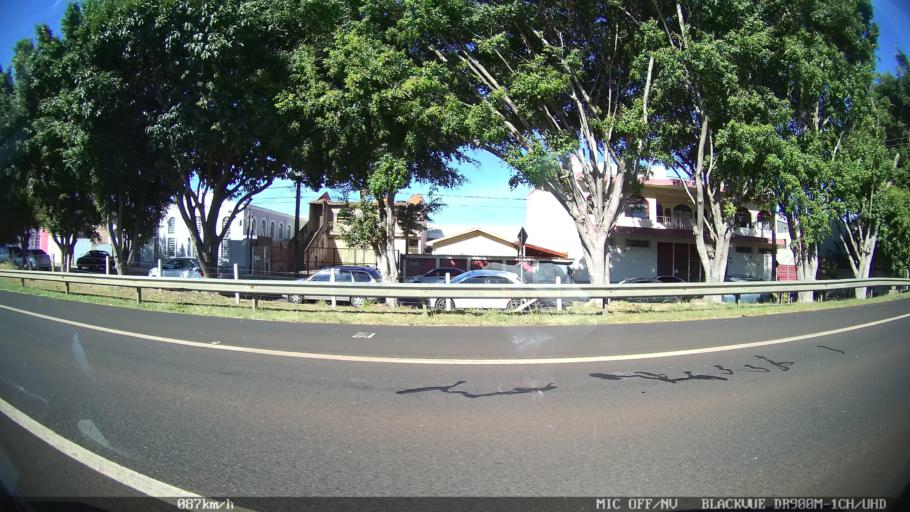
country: BR
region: Sao Paulo
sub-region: Franca
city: Franca
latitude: -20.5740
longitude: -47.3706
